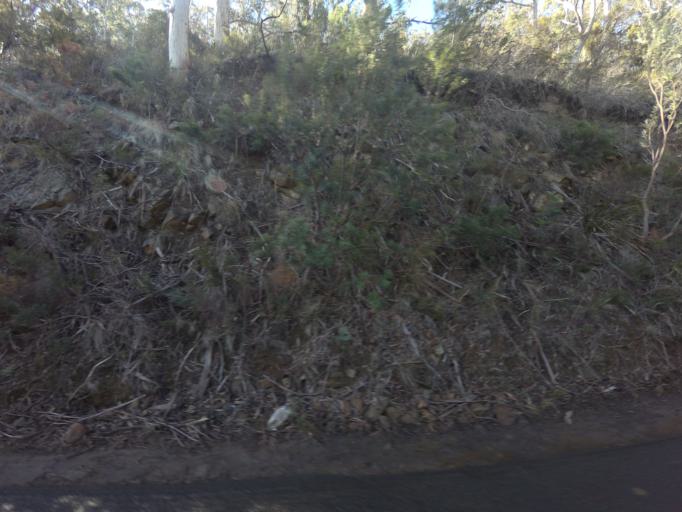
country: AU
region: Tasmania
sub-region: Glenorchy
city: Berriedale
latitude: -42.8202
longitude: 147.1797
